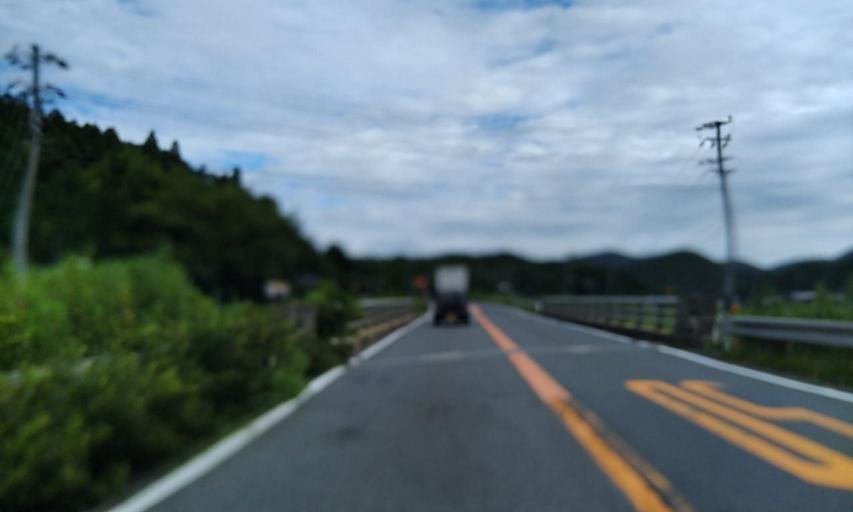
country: JP
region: Kyoto
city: Ayabe
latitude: 35.1799
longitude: 135.3456
